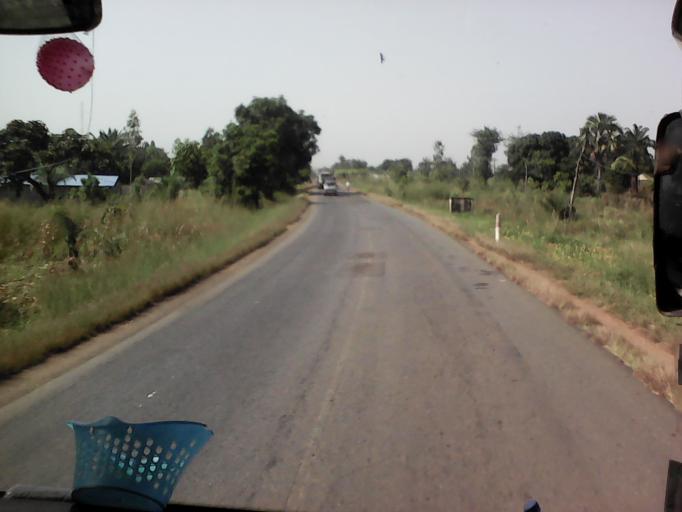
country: TG
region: Centrale
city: Sokode
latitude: 8.9211
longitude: 1.1083
